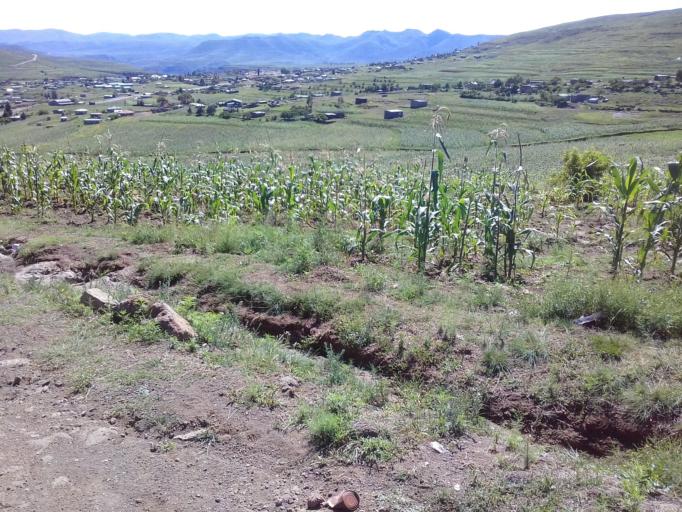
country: LS
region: Thaba-Tseka
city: Thaba-Tseka
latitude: -29.5229
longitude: 28.5830
